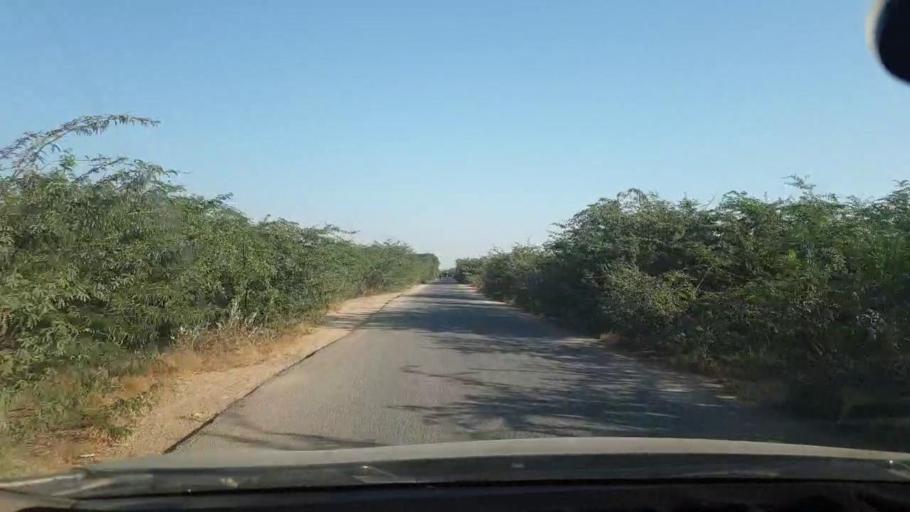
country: PK
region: Sindh
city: Malir Cantonment
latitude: 25.1476
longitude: 67.1881
